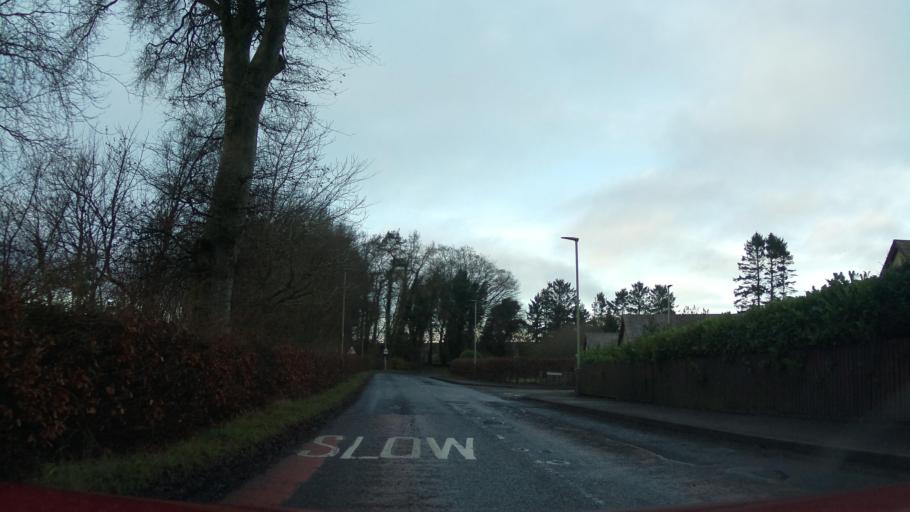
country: GB
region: Scotland
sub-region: Angus
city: Letham
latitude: 56.5322
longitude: -2.7974
